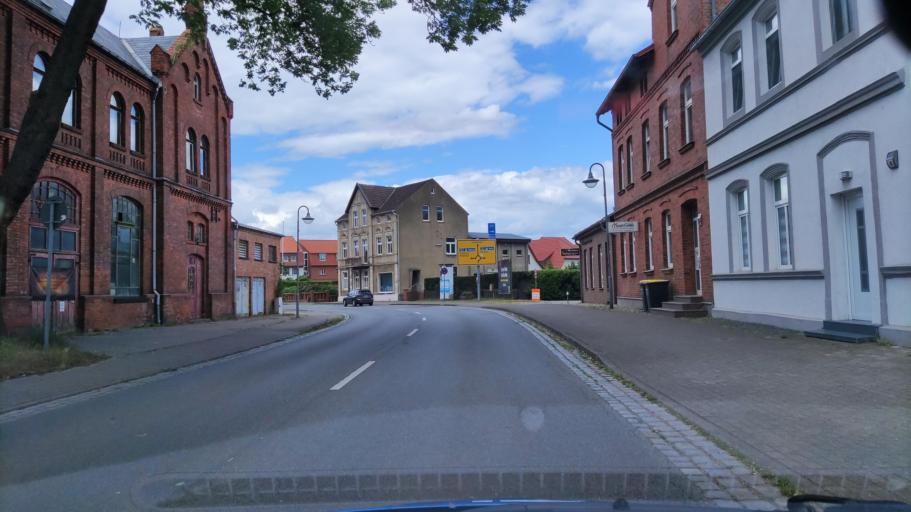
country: DE
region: Mecklenburg-Vorpommern
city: Neustadt-Glewe
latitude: 53.3827
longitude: 11.5809
